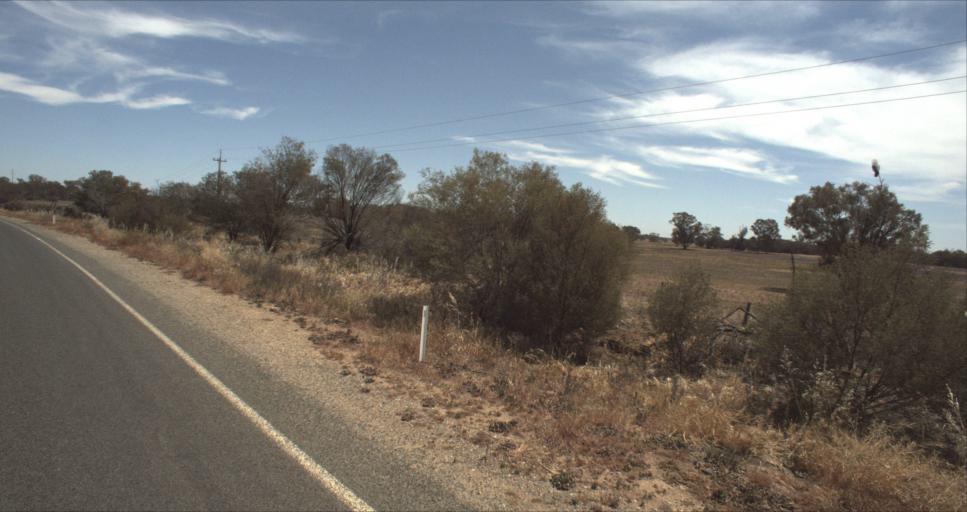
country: AU
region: New South Wales
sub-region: Leeton
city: Leeton
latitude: -34.6602
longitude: 146.4534
